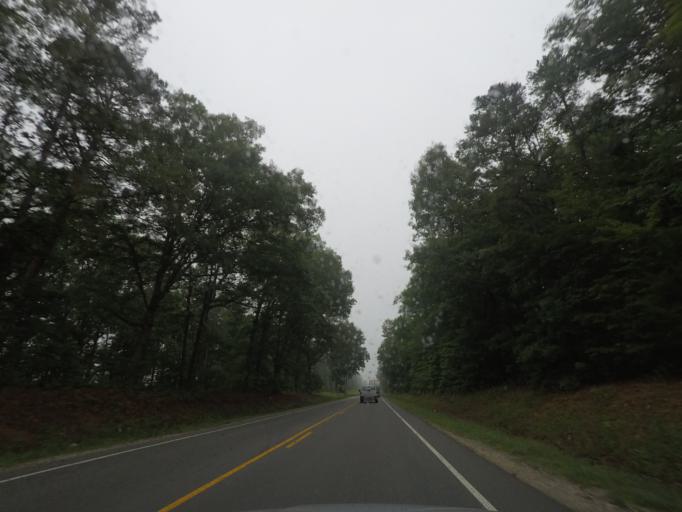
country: US
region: Virginia
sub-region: Buckingham County
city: Buckingham
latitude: 37.4872
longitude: -78.4753
